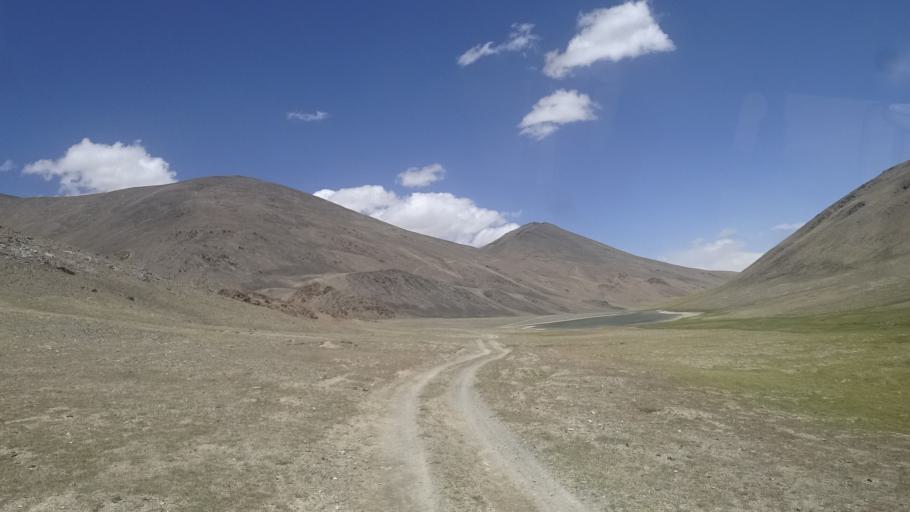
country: TJ
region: Gorno-Badakhshan
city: Murghob
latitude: 37.5190
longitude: 74.0594
